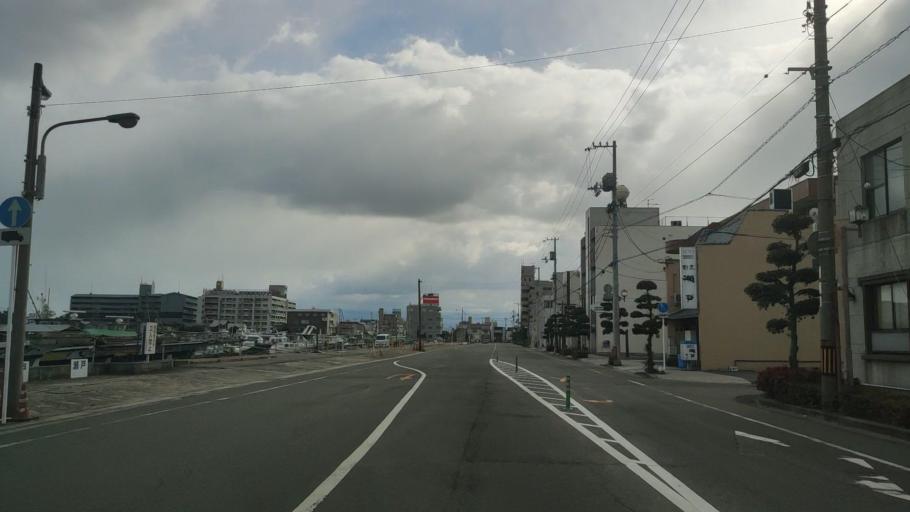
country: JP
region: Ehime
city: Saijo
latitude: 34.0679
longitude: 133.0050
